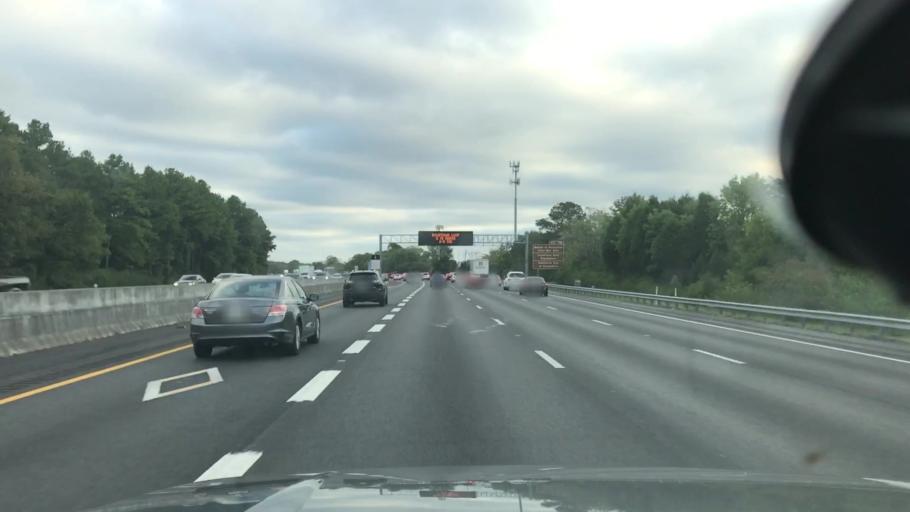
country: US
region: Tennessee
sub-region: Williamson County
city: Brentwood
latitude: 36.0585
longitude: -86.7732
